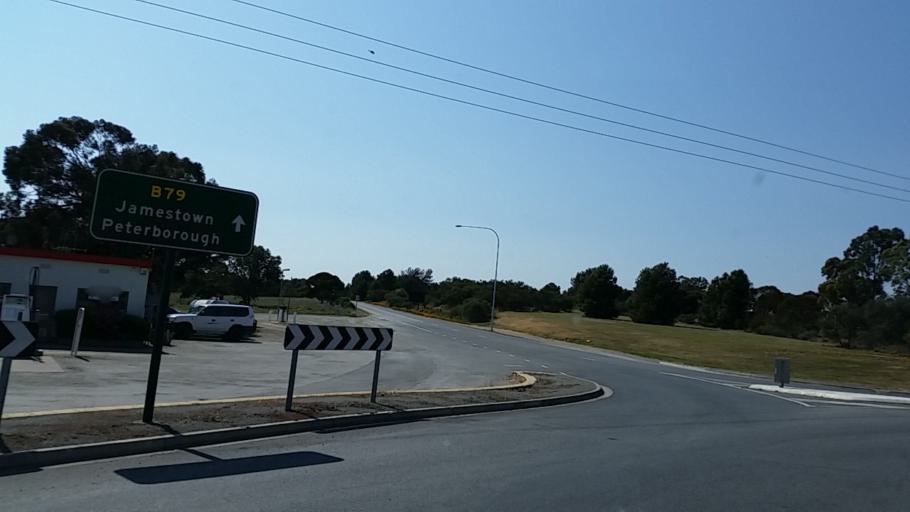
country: AU
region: South Australia
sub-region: Port Pirie City and Dists
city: Crystal Brook
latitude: -33.2647
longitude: 138.3458
